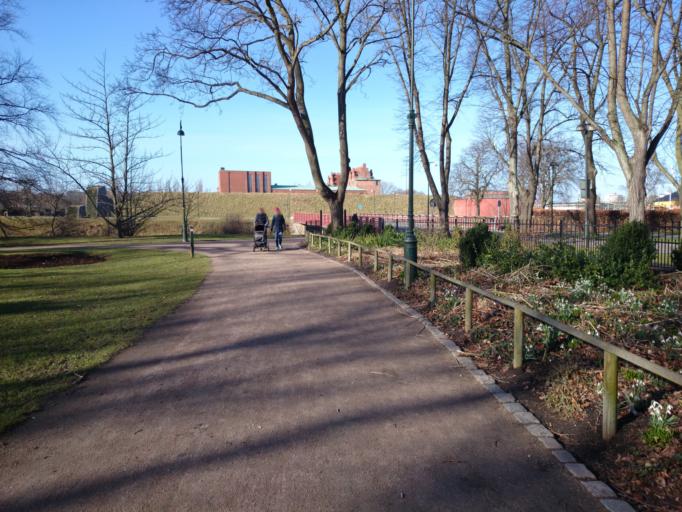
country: SE
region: Skane
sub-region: Malmo
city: Malmoe
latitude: 55.6053
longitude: 12.9914
